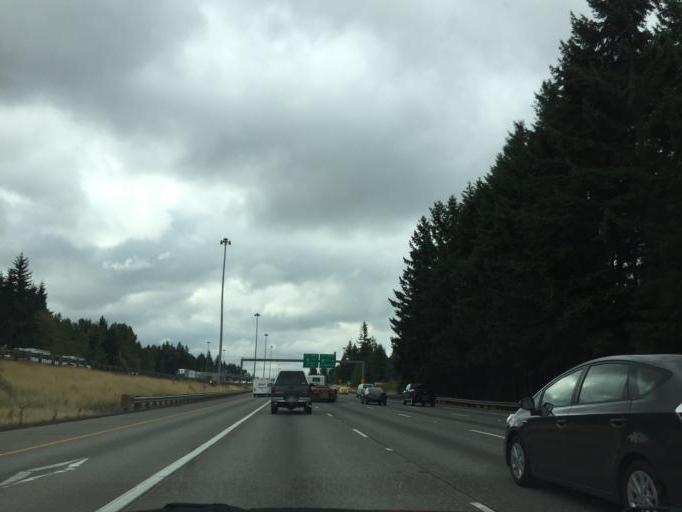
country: US
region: Washington
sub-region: King County
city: Lakeland South
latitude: 47.2956
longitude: -122.3048
